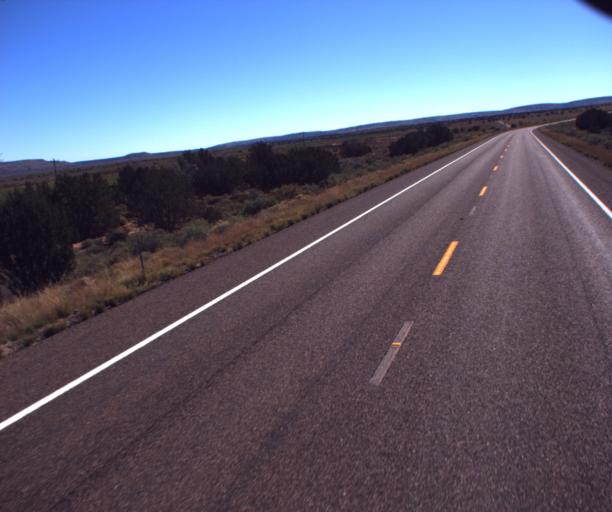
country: US
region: Arizona
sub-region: Apache County
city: Saint Johns
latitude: 34.6166
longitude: -109.6573
